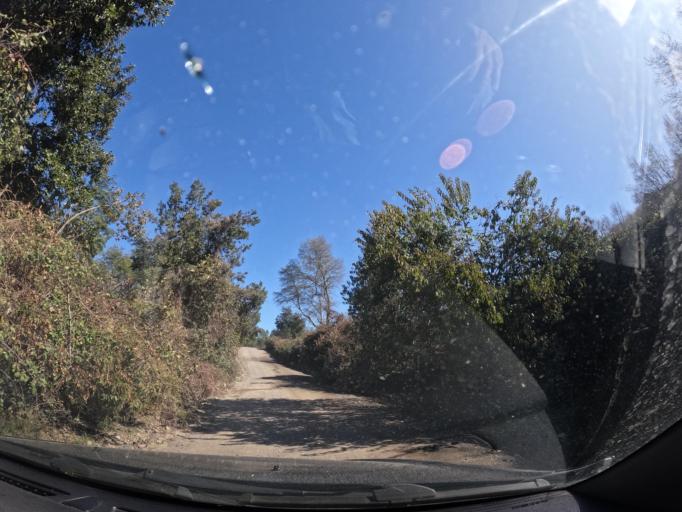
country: CL
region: Maule
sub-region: Provincia de Linares
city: Longavi
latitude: -36.2270
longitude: -71.3801
